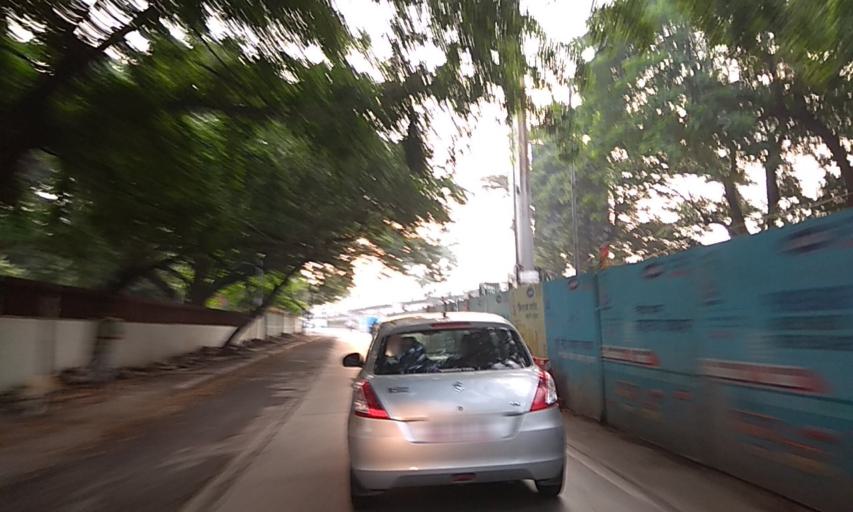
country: IN
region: Maharashtra
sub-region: Pune Division
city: Shivaji Nagar
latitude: 18.5298
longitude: 73.8693
